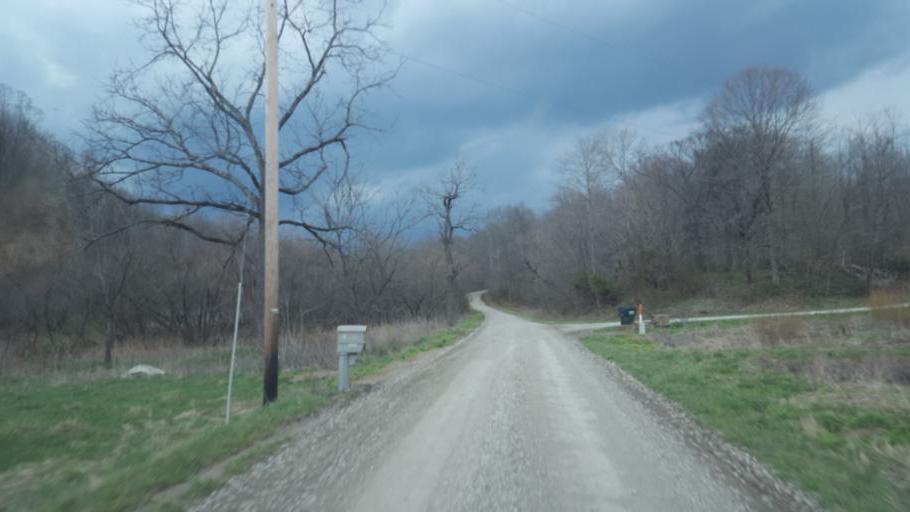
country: US
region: Ohio
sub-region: Guernsey County
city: Mantua
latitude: 40.1105
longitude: -81.8097
